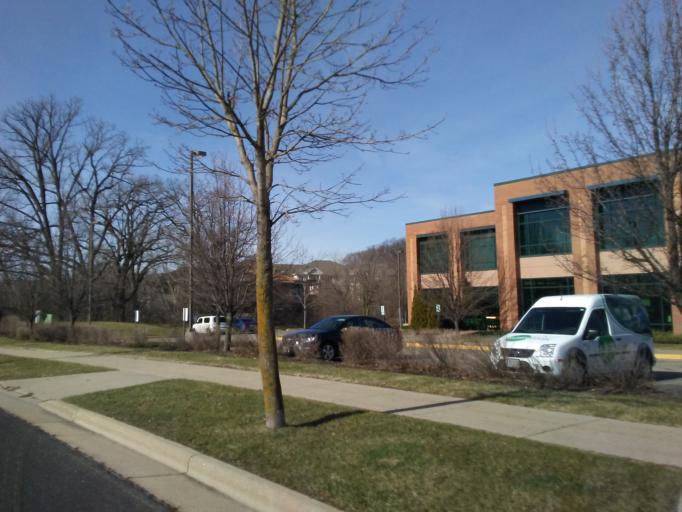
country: US
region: Wisconsin
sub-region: Dane County
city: Middleton
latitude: 43.0899
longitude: -89.5311
